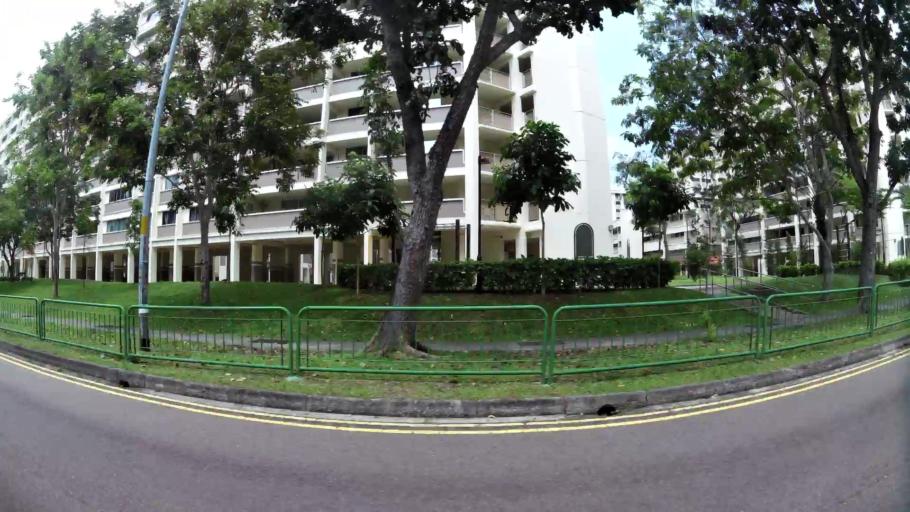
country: SG
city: Singapore
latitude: 1.3318
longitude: 103.9113
